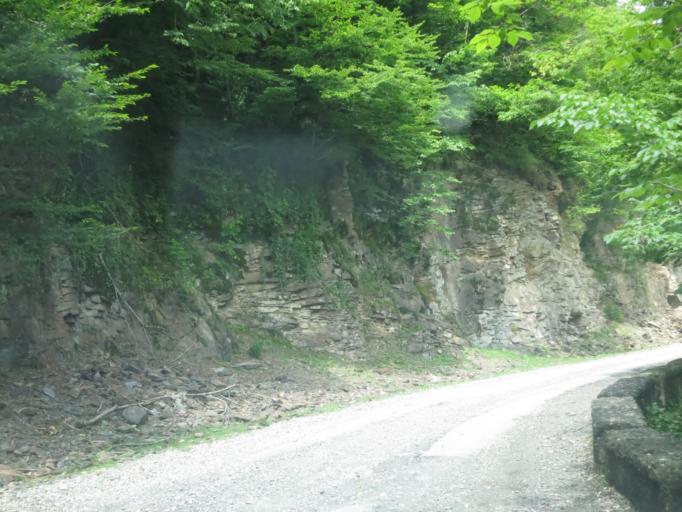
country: GE
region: Kakheti
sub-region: Telavi
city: Telavi
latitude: 42.1847
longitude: 45.4417
